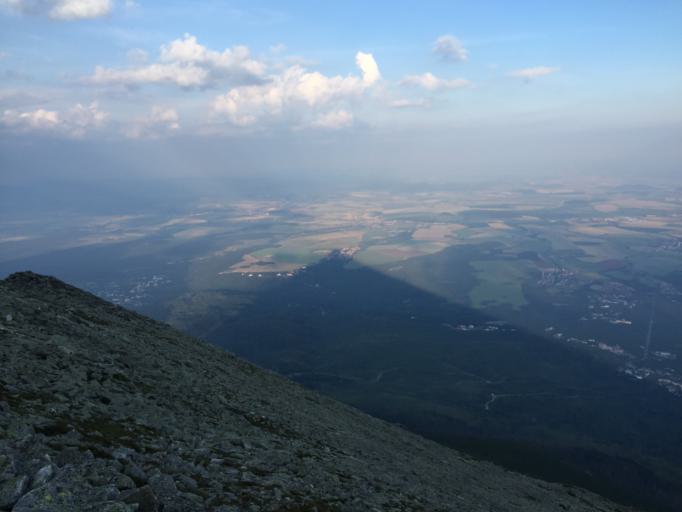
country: SK
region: Presovsky
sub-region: Okres Poprad
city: Vysoke Tatry
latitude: 49.1635
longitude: 20.1921
